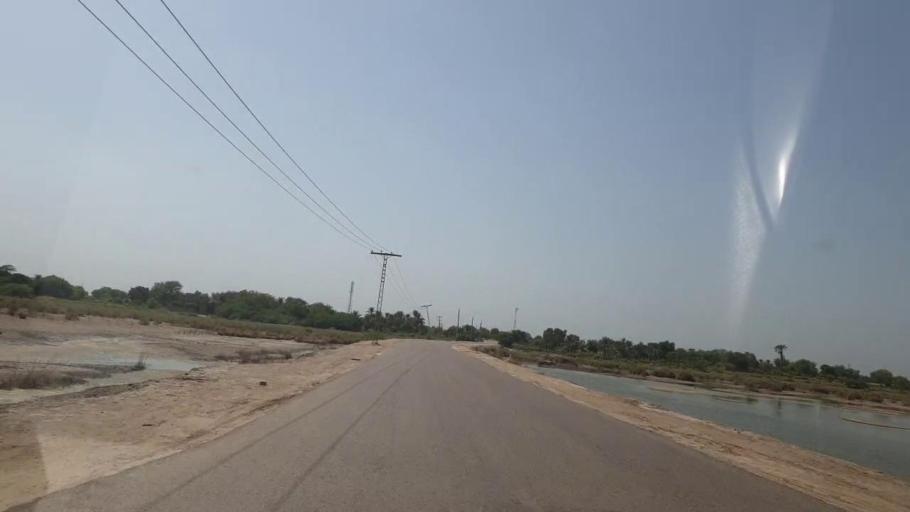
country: PK
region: Sindh
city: Bozdar
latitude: 27.1252
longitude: 68.5400
